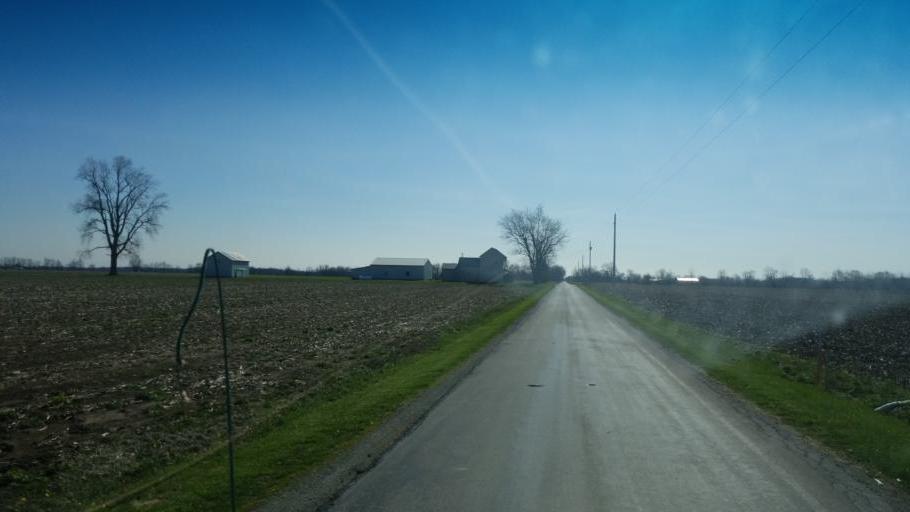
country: US
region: Ohio
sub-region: Hardin County
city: Forest
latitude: 40.7085
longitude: -83.4955
